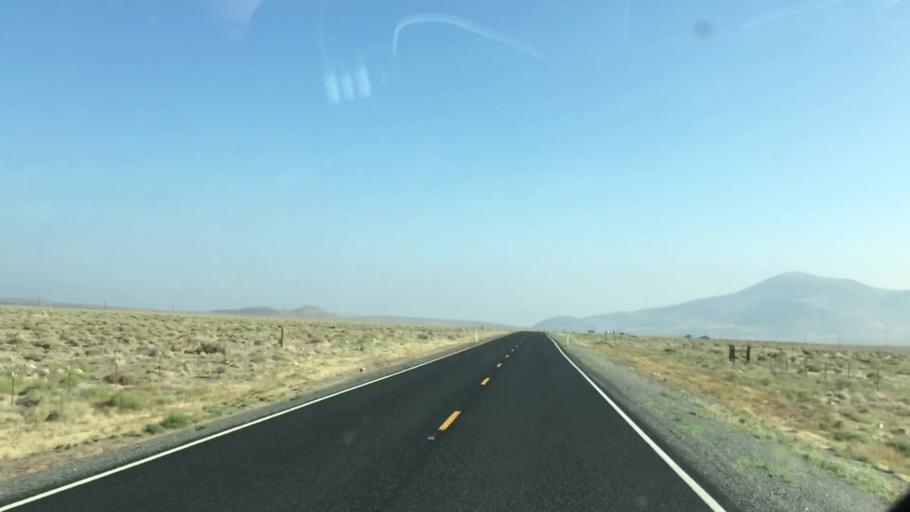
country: US
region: Nevada
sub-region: Lyon County
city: Fernley
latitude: 39.7204
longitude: -119.3344
